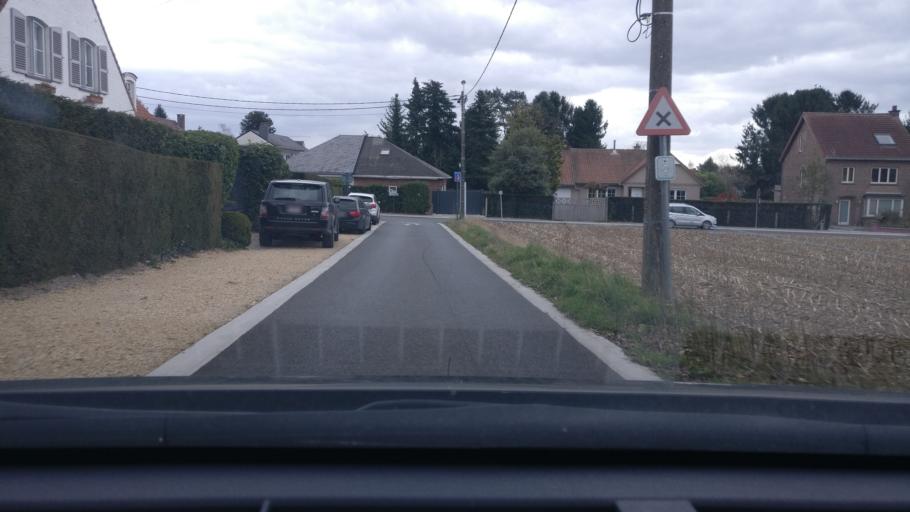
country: BE
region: Flanders
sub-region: Provincie Vlaams-Brabant
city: Tervuren
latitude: 50.7928
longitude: 4.5043
